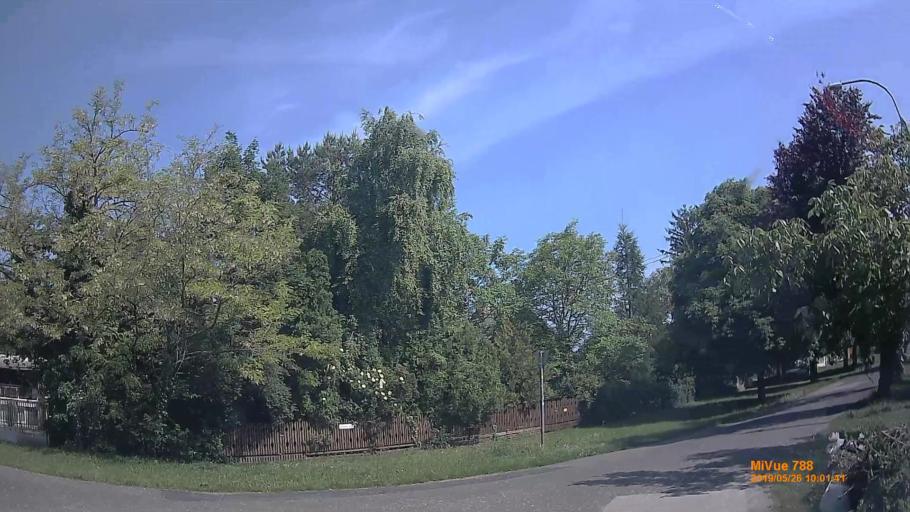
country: HU
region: Somogy
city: Balatonszabadi
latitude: 46.9395
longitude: 18.1354
